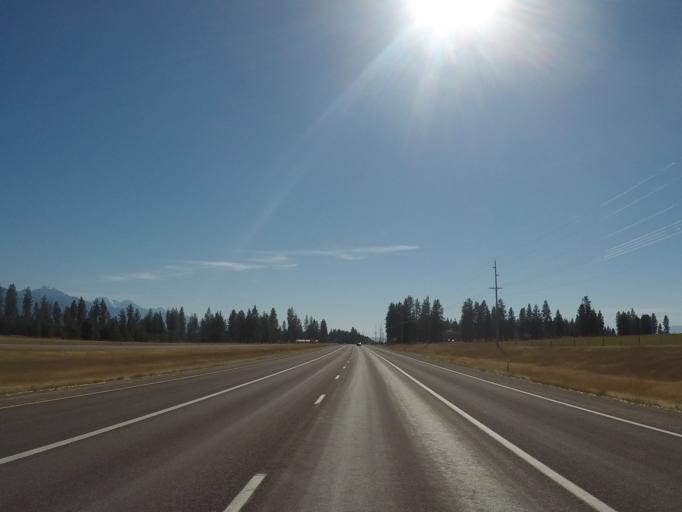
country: US
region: Montana
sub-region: Lake County
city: Pablo
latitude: 47.6306
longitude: -114.1142
